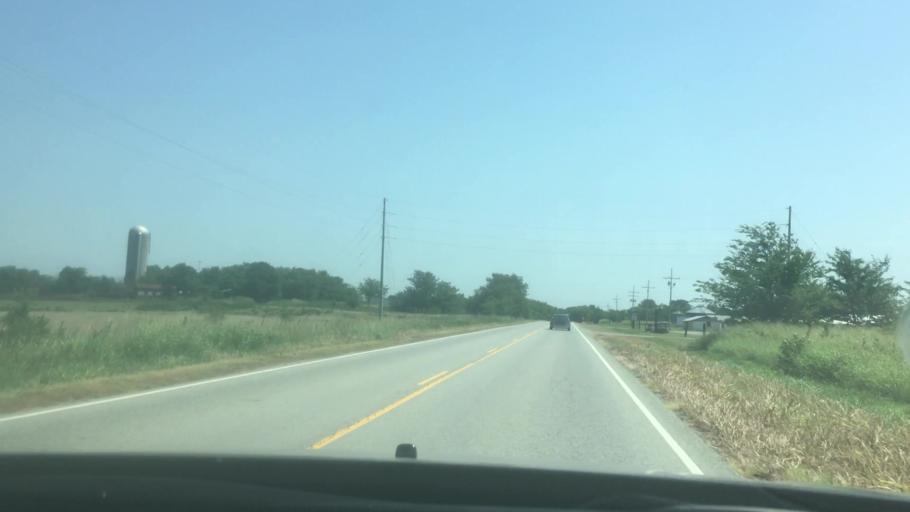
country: US
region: Oklahoma
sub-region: Coal County
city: Coalgate
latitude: 34.4954
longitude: -96.4135
